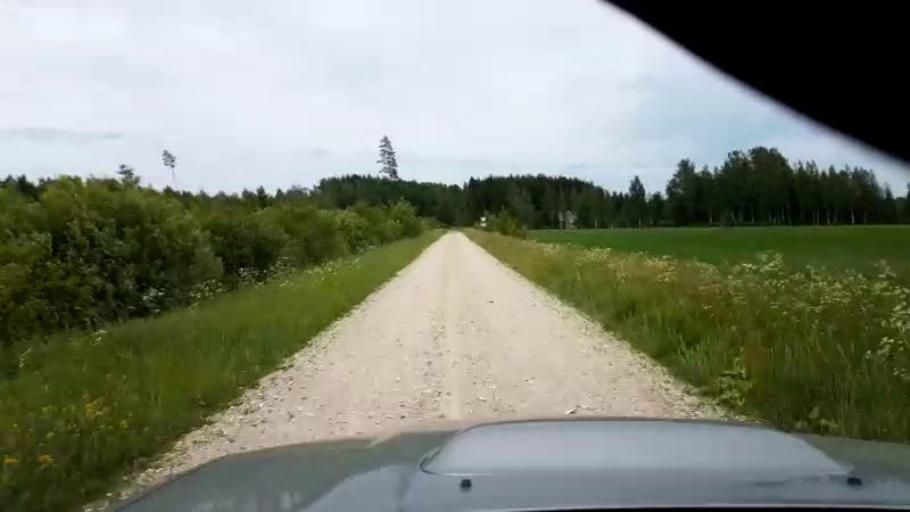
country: EE
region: Paernumaa
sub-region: Sindi linn
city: Sindi
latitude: 58.5234
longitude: 24.6259
